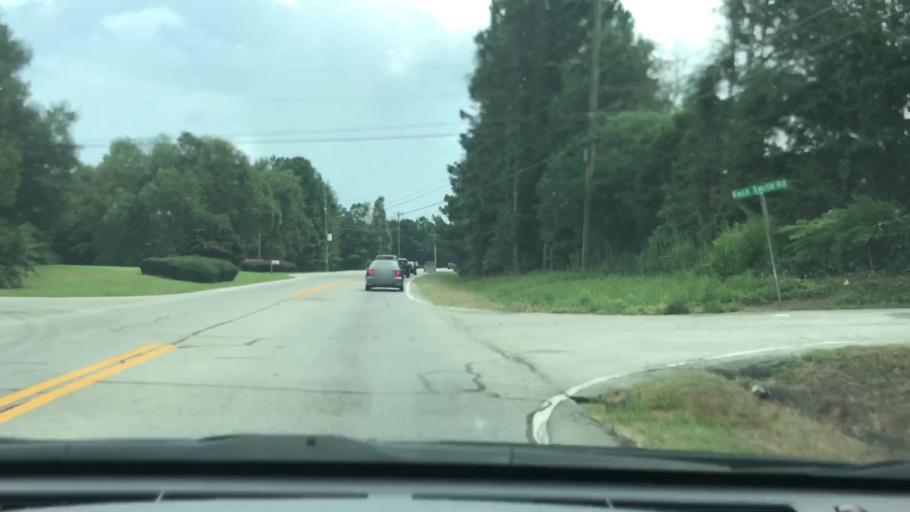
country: US
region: Georgia
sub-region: Walton County
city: Walnut Grove
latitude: 33.7918
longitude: -83.8602
